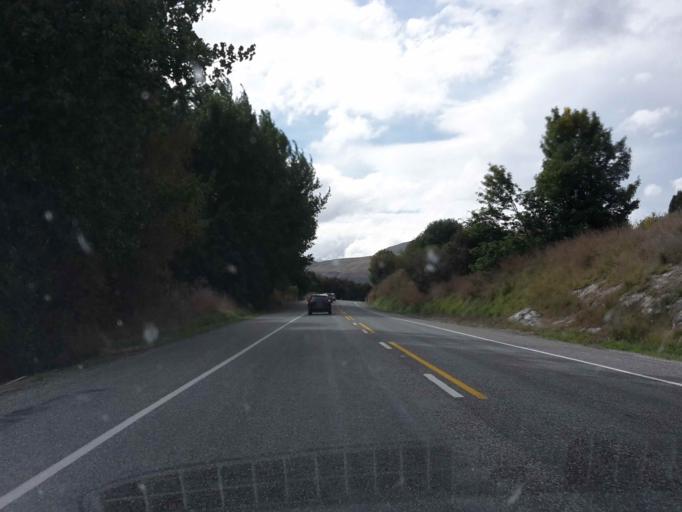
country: NZ
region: Otago
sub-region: Queenstown-Lakes District
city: Arrowtown
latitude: -44.9825
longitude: 168.8220
